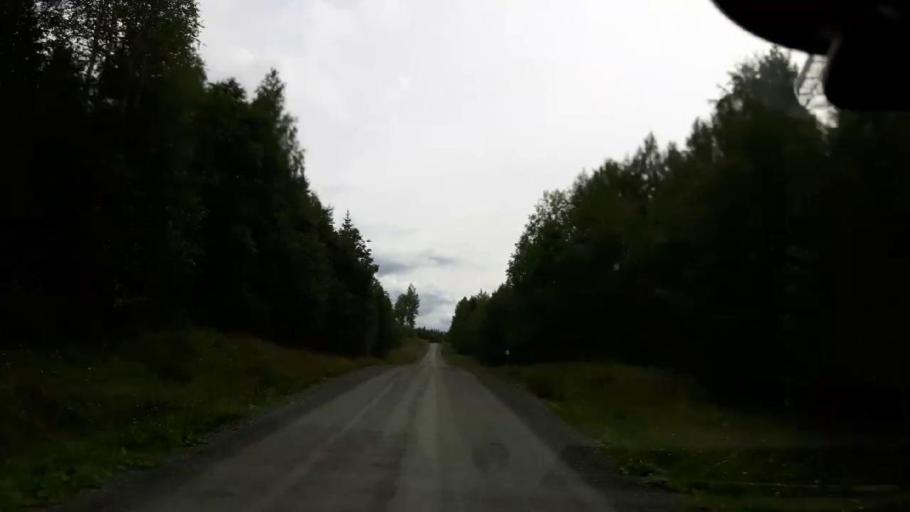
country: SE
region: Jaemtland
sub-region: Krokoms Kommun
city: Valla
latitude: 63.6547
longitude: 13.9794
